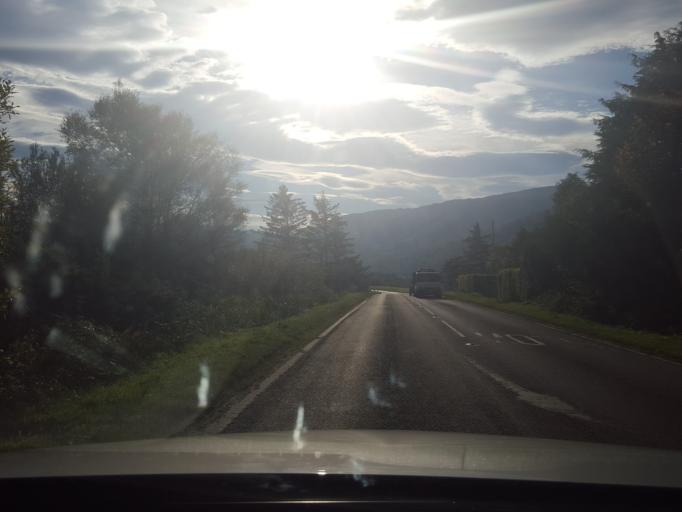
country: GB
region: Scotland
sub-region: Highland
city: Fort William
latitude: 57.2824
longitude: -5.5229
